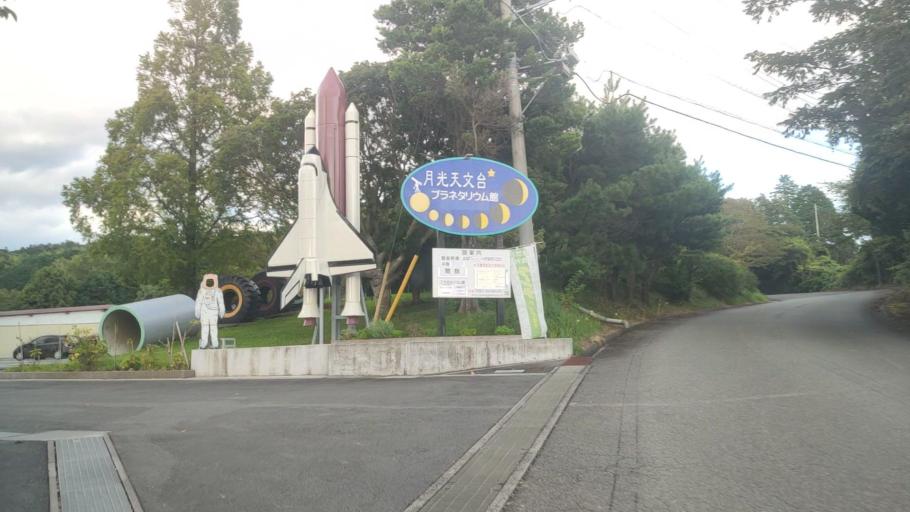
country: JP
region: Kanagawa
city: Hakone
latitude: 35.1282
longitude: 138.9925
